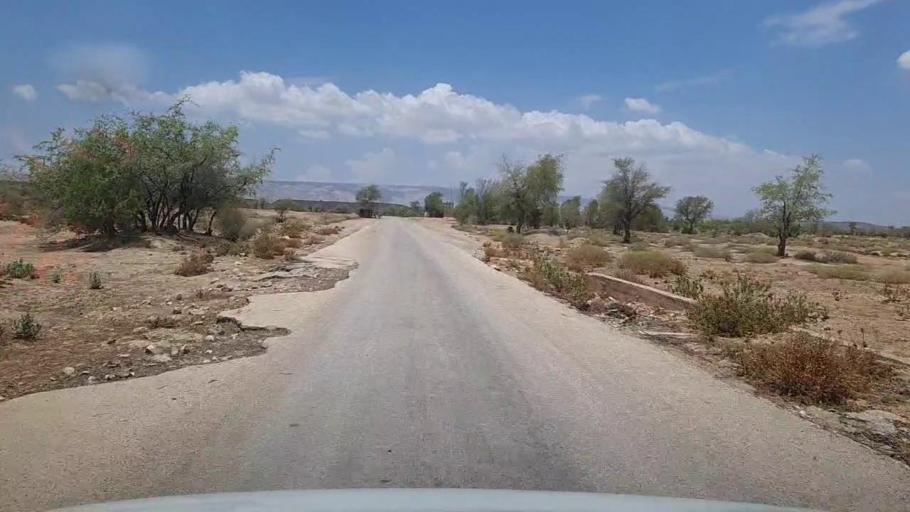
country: PK
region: Sindh
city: Bhan
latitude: 26.3175
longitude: 67.6021
